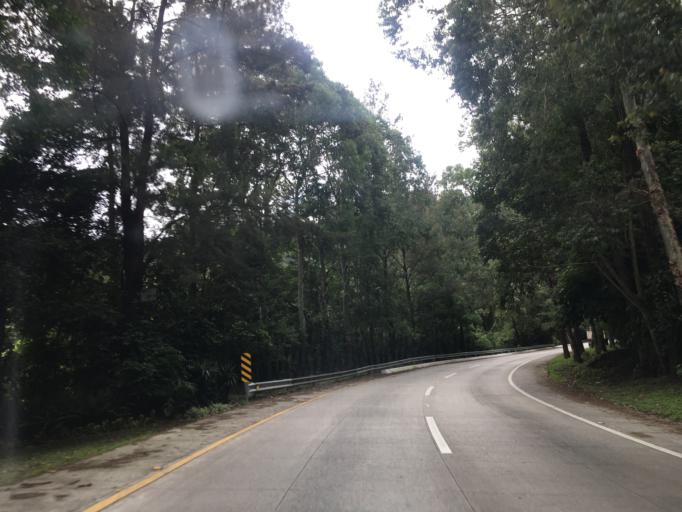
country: GT
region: Sacatepequez
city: Santa Lucia Milpas Altas
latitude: 14.5611
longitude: -90.7013
